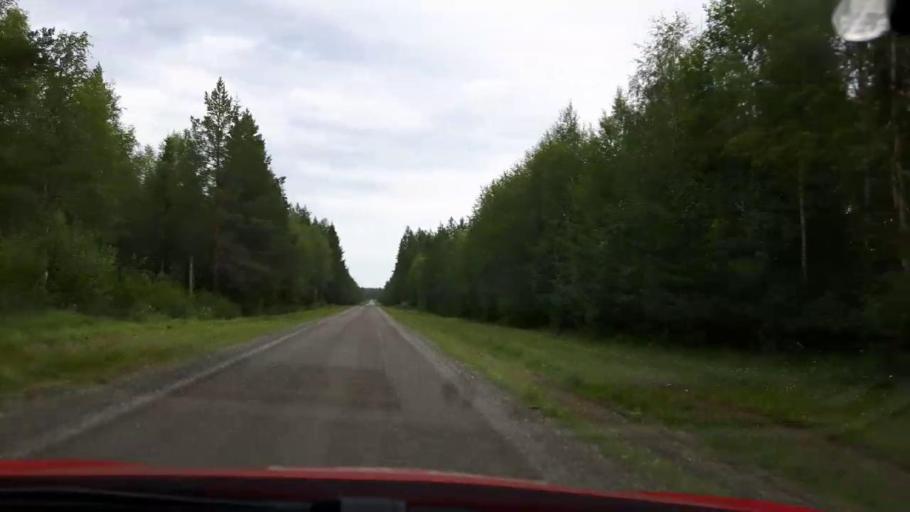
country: SE
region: Jaemtland
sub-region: Stroemsunds Kommun
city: Stroemsund
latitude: 63.7289
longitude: 15.5475
